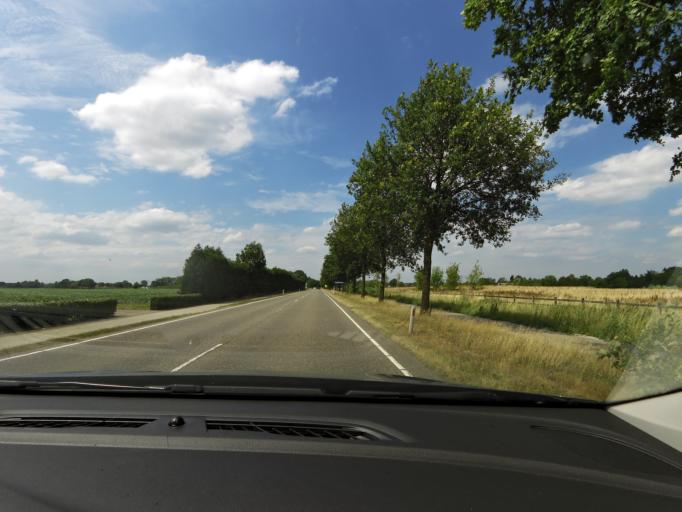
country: NL
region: North Brabant
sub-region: Gemeente Baarle-Nassau
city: Baarle-Nassau
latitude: 51.4877
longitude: 4.8814
